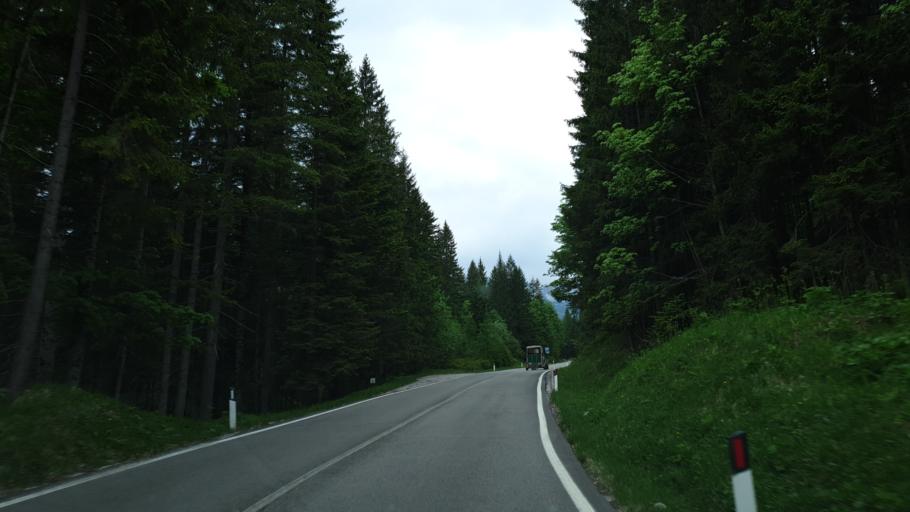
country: IT
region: Veneto
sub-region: Provincia di Belluno
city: San Vito
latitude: 46.5376
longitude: 12.2567
